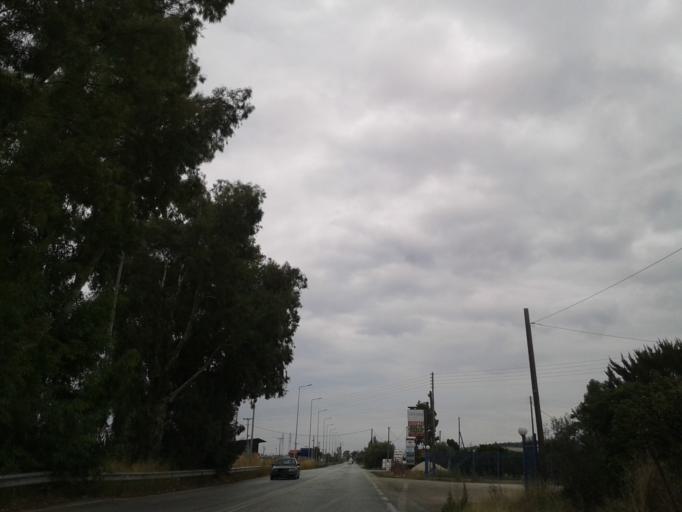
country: GR
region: Peloponnese
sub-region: Nomos Argolidos
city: Koutsopodi
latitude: 37.6655
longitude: 22.7241
